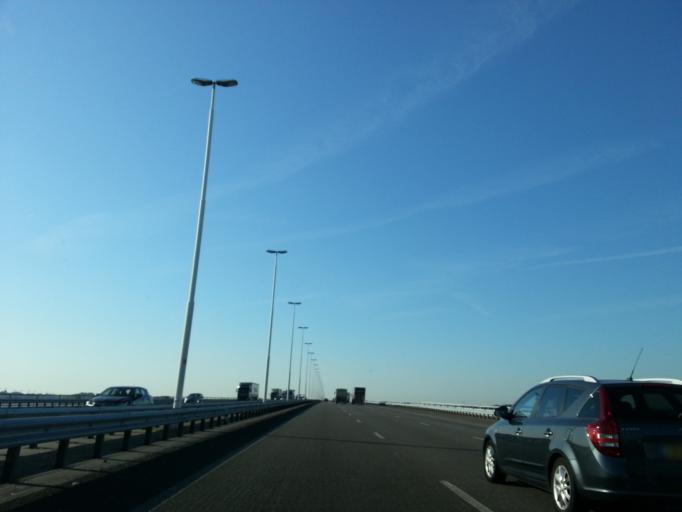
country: NL
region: South Holland
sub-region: Gemeente Strijen
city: Strijen
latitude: 51.7208
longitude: 4.6345
